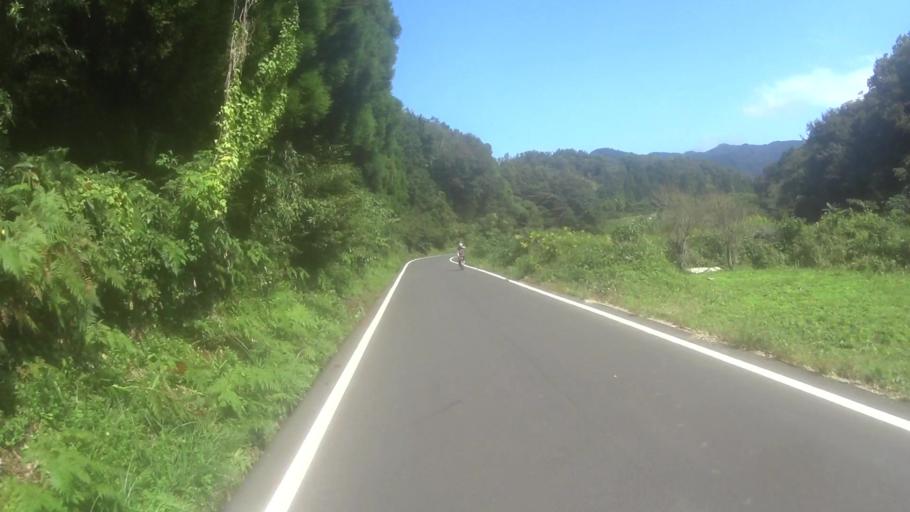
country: JP
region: Kyoto
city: Miyazu
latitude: 35.6121
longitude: 135.1175
